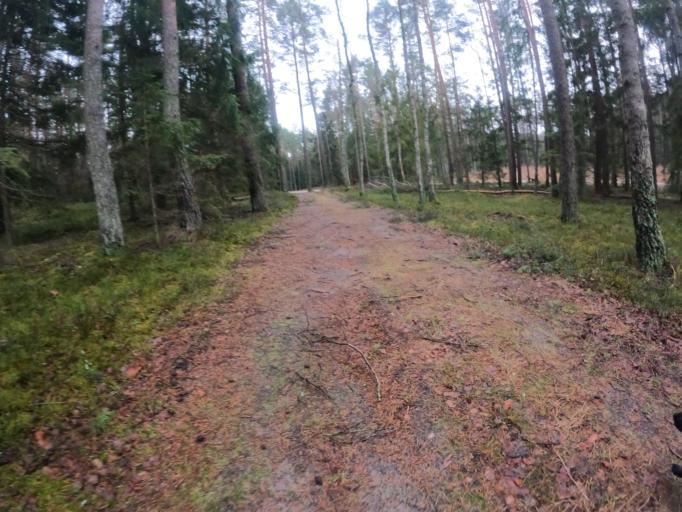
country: PL
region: West Pomeranian Voivodeship
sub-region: Powiat koszalinski
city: Polanow
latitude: 54.2401
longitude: 16.7015
